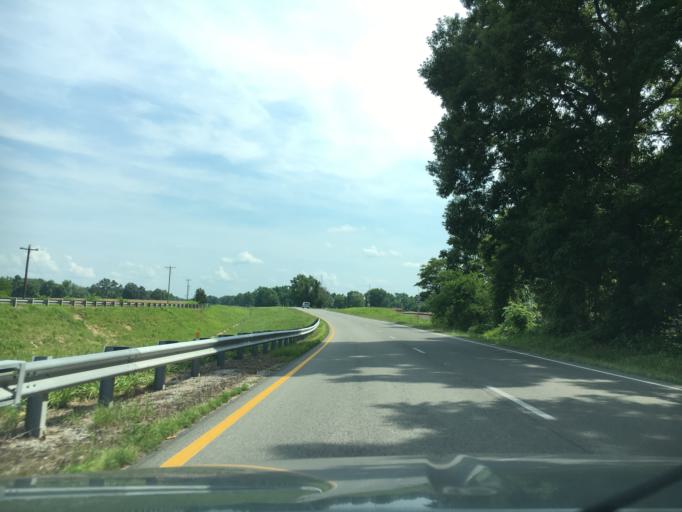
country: US
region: Virginia
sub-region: Nottoway County
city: Crewe
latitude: 37.2399
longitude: -78.1456
